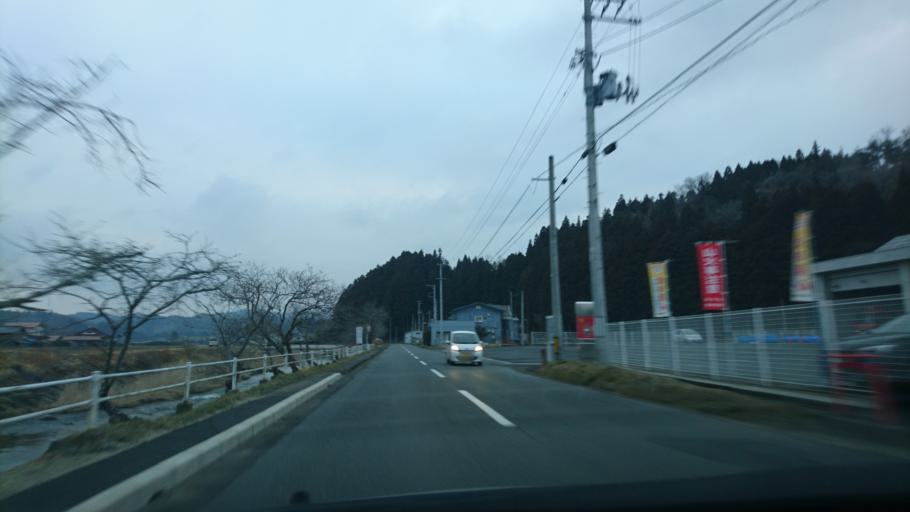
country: JP
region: Iwate
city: Ichinoseki
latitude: 39.0197
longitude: 141.3373
